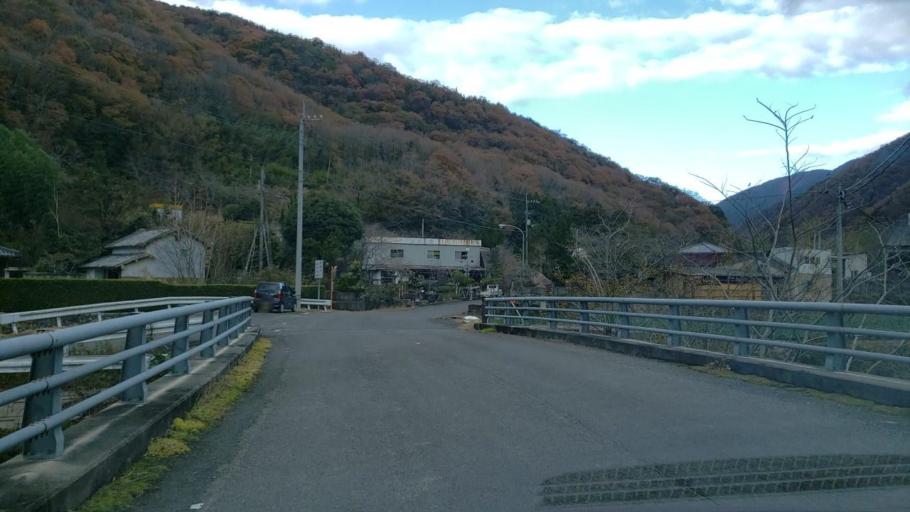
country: JP
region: Tokushima
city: Wakimachi
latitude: 34.1113
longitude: 134.2241
